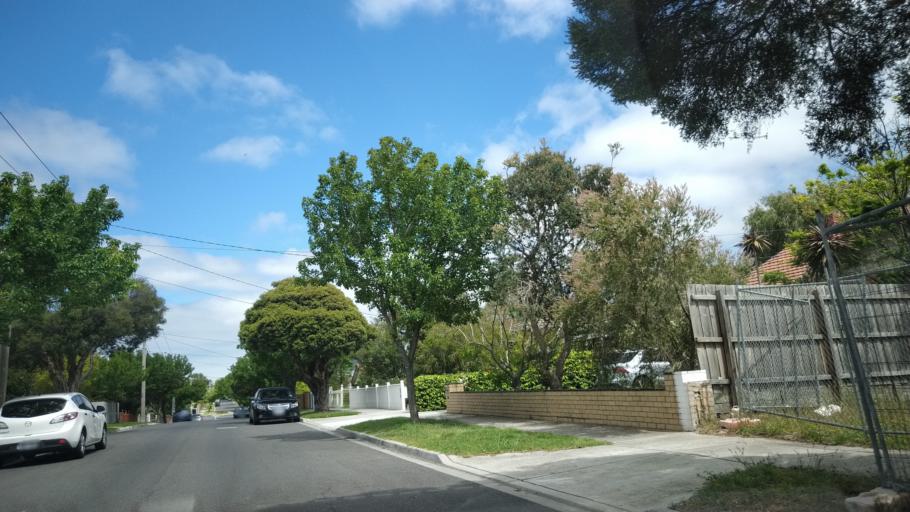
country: AU
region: Victoria
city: Murrumbeena
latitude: -37.8983
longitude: 145.0697
